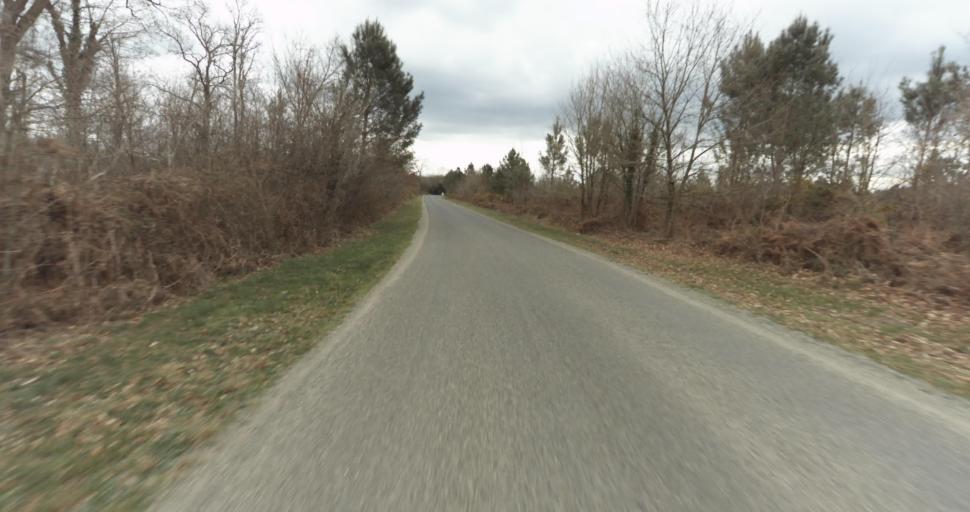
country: FR
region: Aquitaine
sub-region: Departement des Landes
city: Roquefort
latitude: 44.0174
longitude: -0.3437
